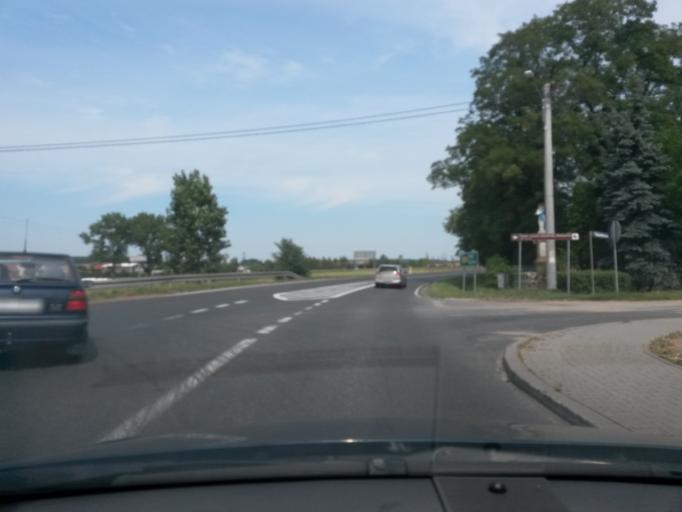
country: PL
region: Greater Poland Voivodeship
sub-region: Powiat gostynski
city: Gostyn
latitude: 51.9356
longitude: 17.0182
